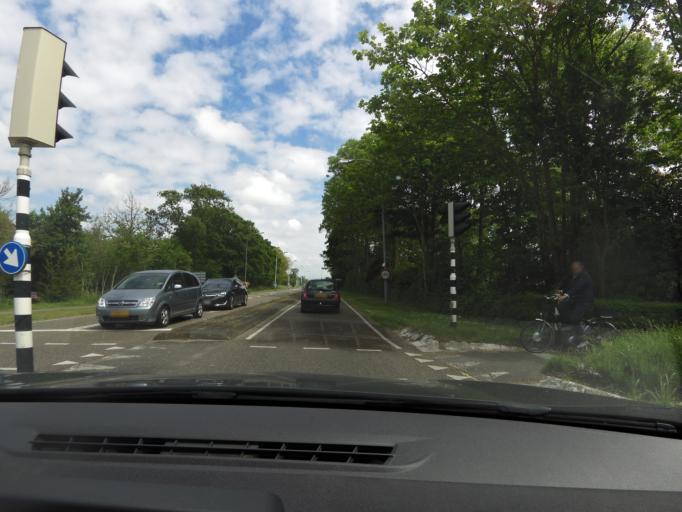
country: NL
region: Zeeland
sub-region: Schouwen-Duiveland
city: Haamstede
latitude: 51.7004
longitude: 3.7428
